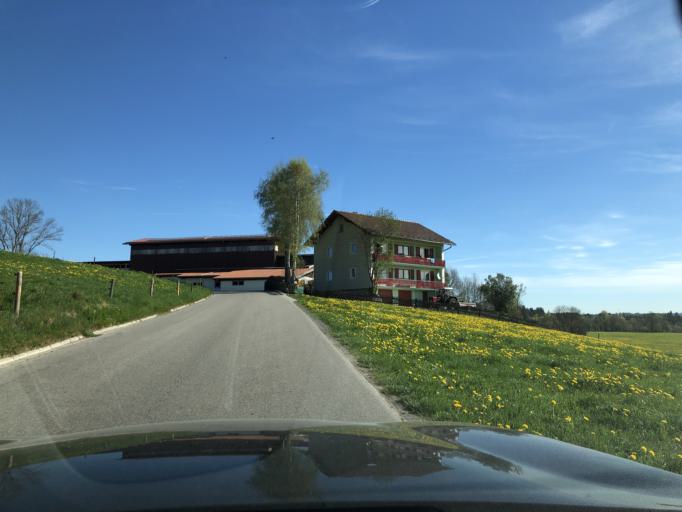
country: DE
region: Bavaria
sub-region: Swabia
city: Wald
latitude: 47.7551
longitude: 10.5691
